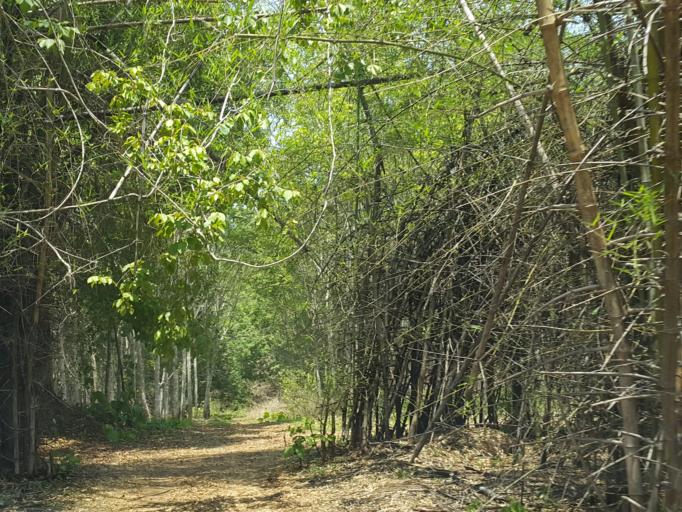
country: TH
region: Kanchanaburi
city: Sai Yok
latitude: 14.2139
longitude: 98.8772
